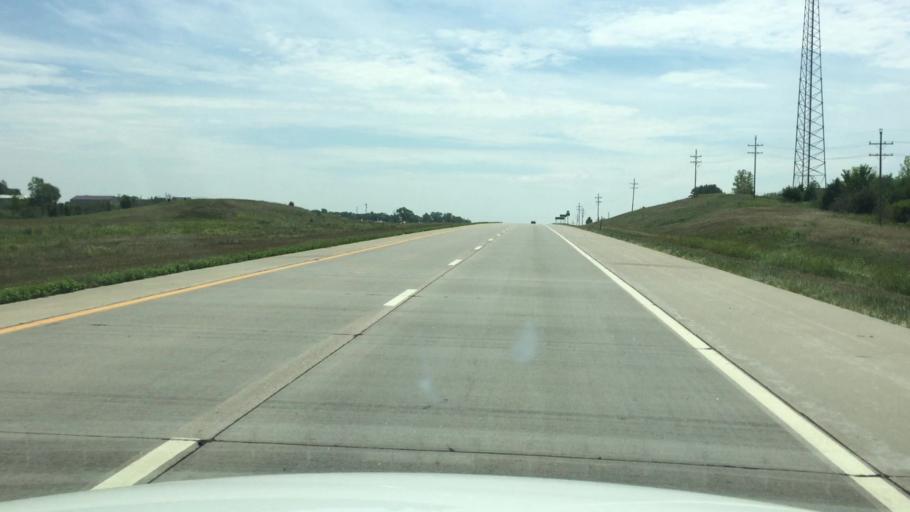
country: US
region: Kansas
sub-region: Shawnee County
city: Silver Lake
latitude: 39.2501
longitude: -95.7197
